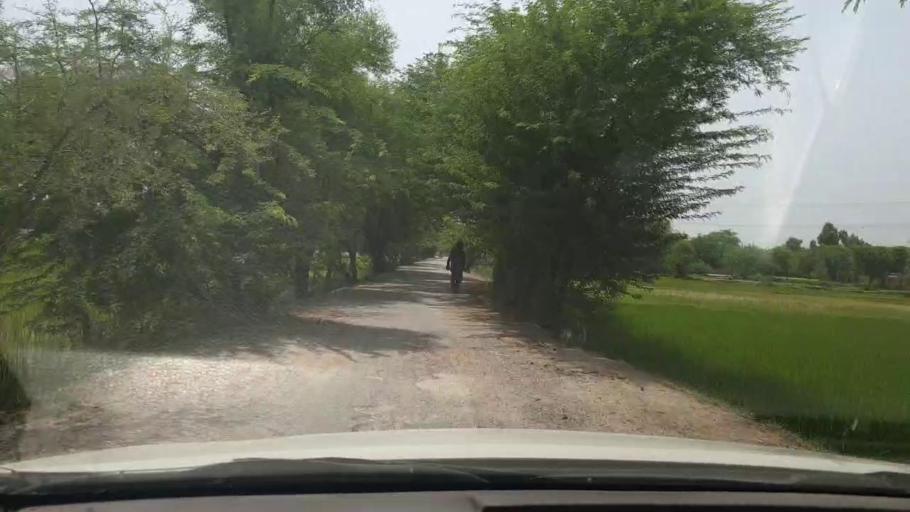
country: PK
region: Sindh
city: Shikarpur
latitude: 28.0205
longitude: 68.6471
